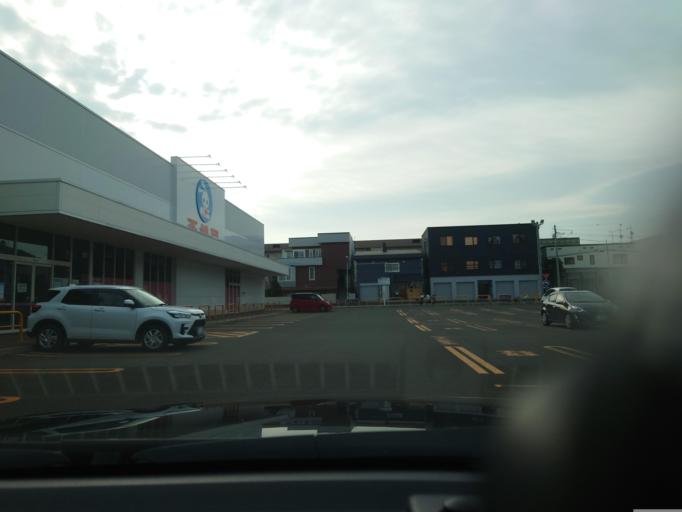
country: JP
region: Hokkaido
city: Sapporo
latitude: 43.0298
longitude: 141.3516
